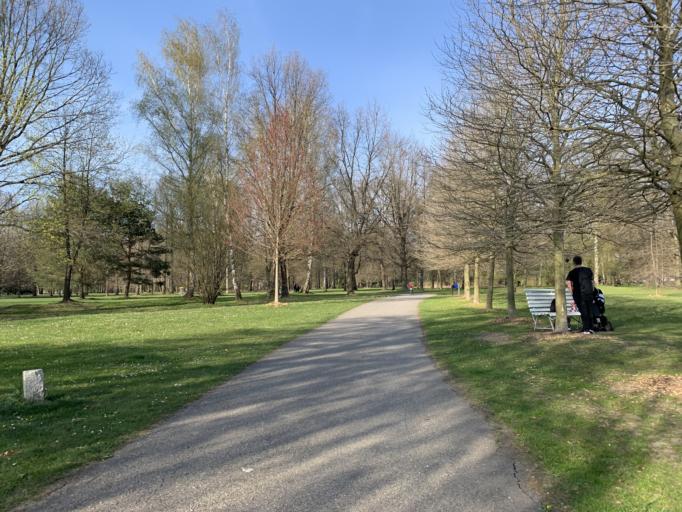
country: CZ
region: Jihocesky
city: Litvinovice
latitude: 48.9669
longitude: 14.4549
